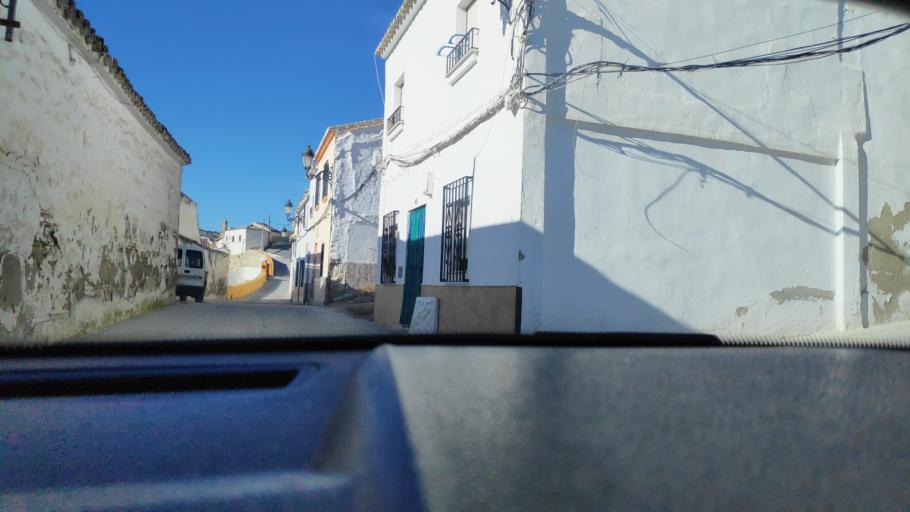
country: ES
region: Andalusia
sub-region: Province of Cordoba
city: Baena
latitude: 37.6118
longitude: -4.3245
